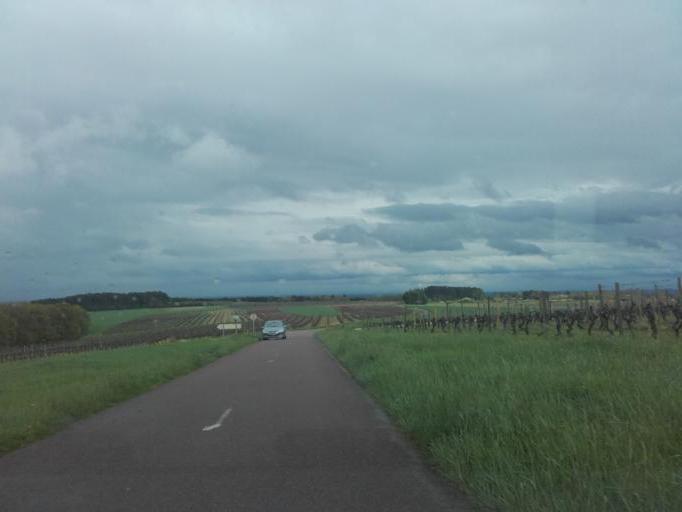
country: FR
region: Bourgogne
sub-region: Departement de la Cote-d'Or
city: Nuits-Saint-Georges
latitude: 47.1037
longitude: 4.8863
